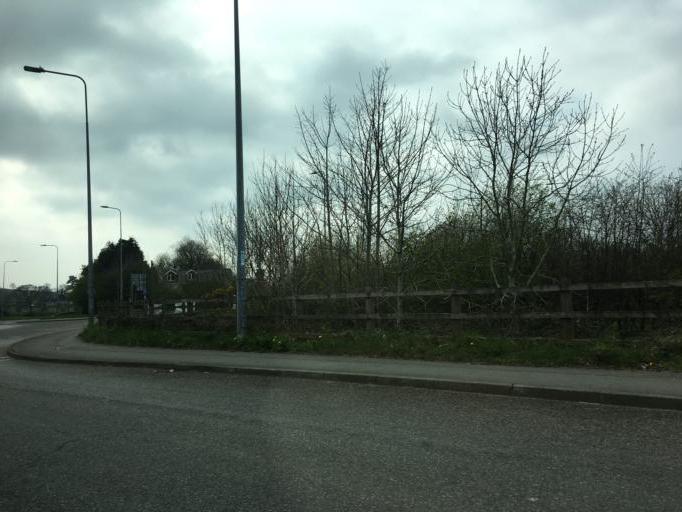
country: GB
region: Wales
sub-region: Gwynedd
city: Y Felinheli
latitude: 53.1685
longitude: -4.2375
